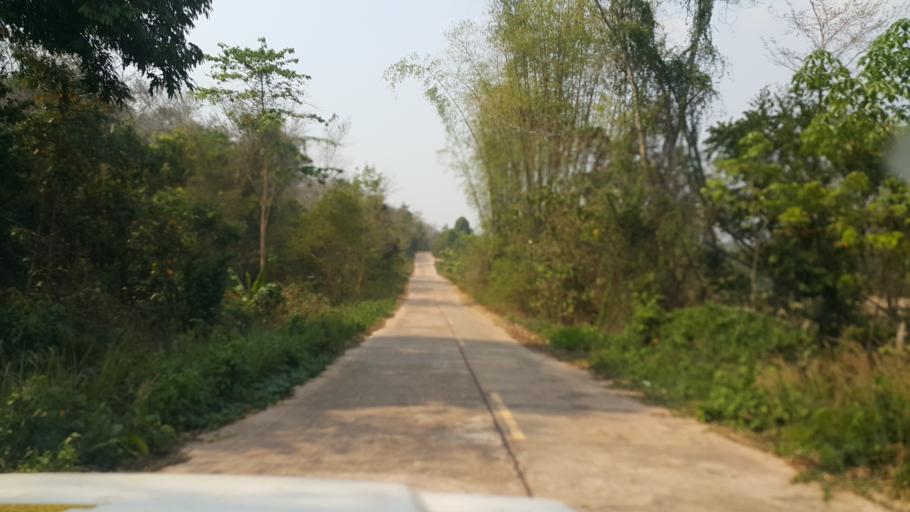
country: TH
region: Nakhon Phanom
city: Ban Phaeng
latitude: 17.9588
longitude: 104.1571
